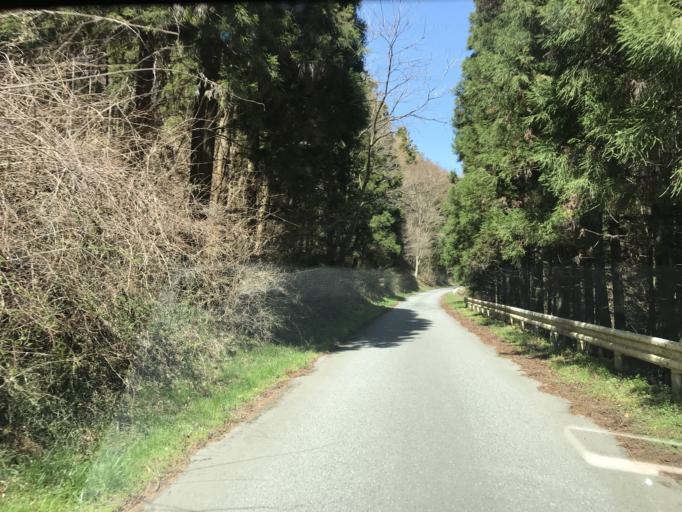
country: JP
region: Iwate
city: Ichinoseki
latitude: 38.8177
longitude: 141.2811
